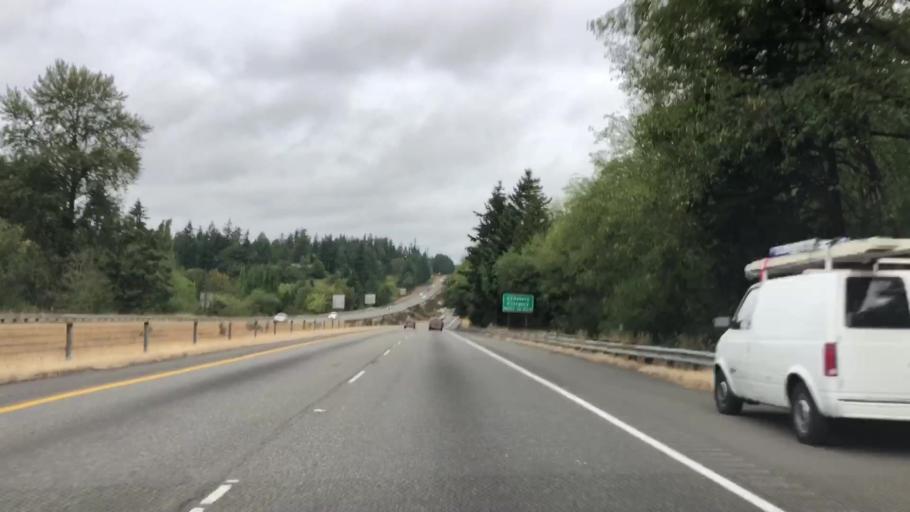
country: US
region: Washington
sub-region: Pierce County
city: Gig Harbor
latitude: 47.3275
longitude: -122.5960
